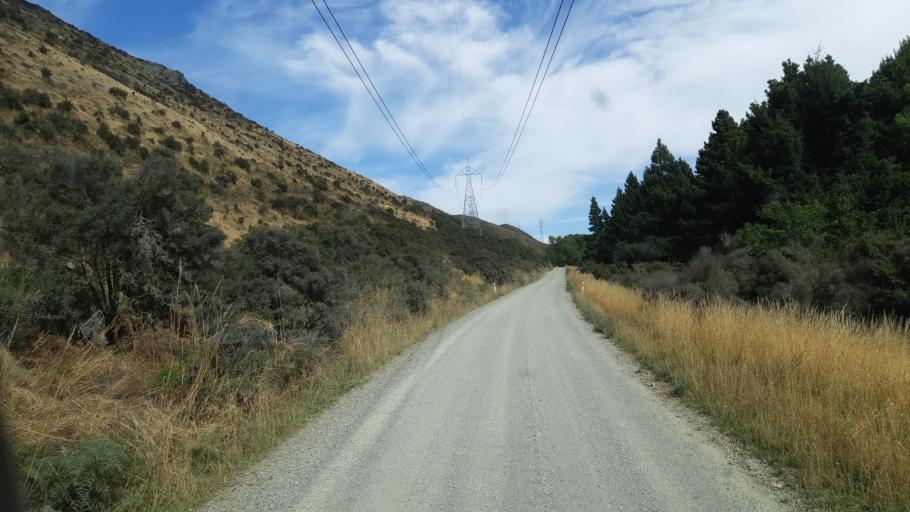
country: NZ
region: Canterbury
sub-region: Timaru District
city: Pleasant Point
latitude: -44.1939
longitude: 170.6398
